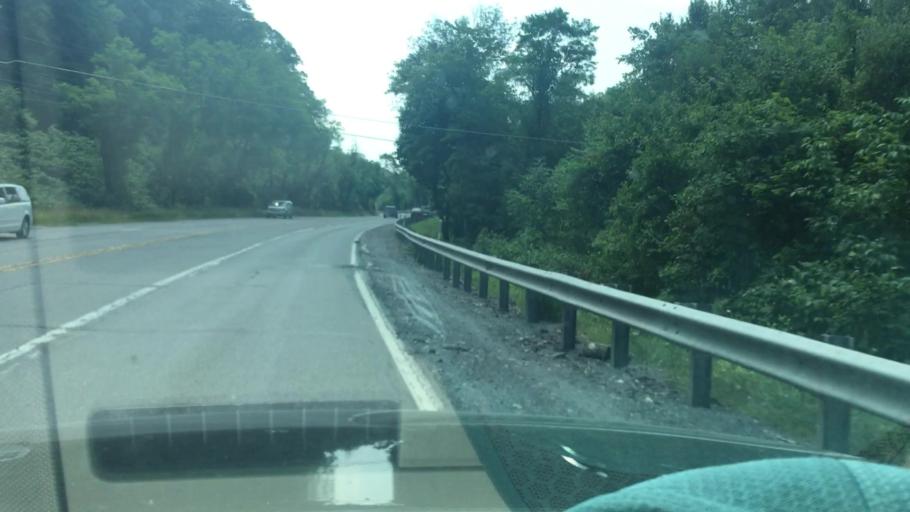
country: US
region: Pennsylvania
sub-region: Schuylkill County
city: Tamaqua
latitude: 40.7862
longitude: -75.9630
